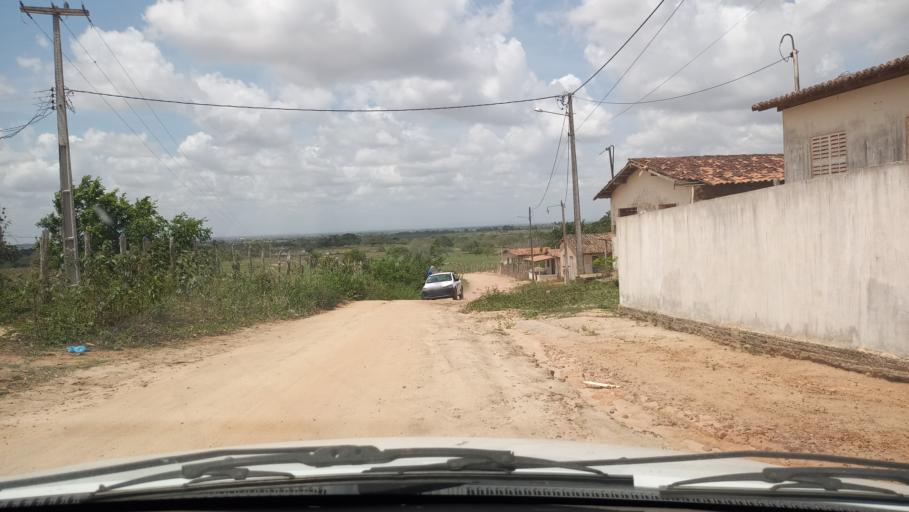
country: BR
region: Rio Grande do Norte
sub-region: Brejinho
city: Brejinho
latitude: -6.2650
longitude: -35.3429
